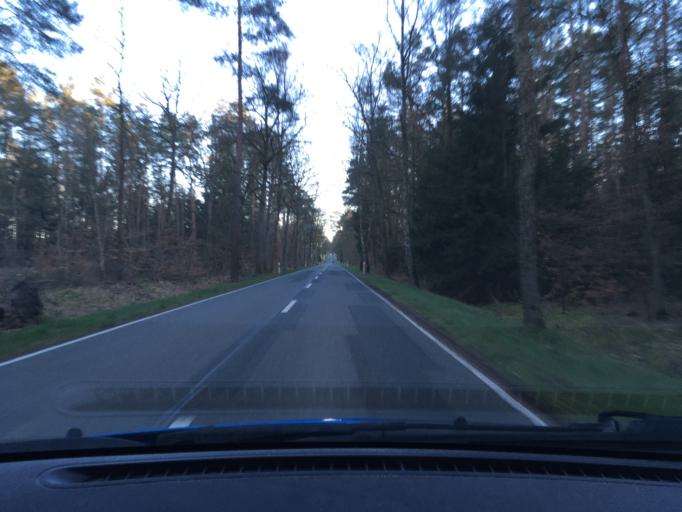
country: DE
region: Lower Saxony
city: Bleckede
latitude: 53.2548
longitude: 10.7444
